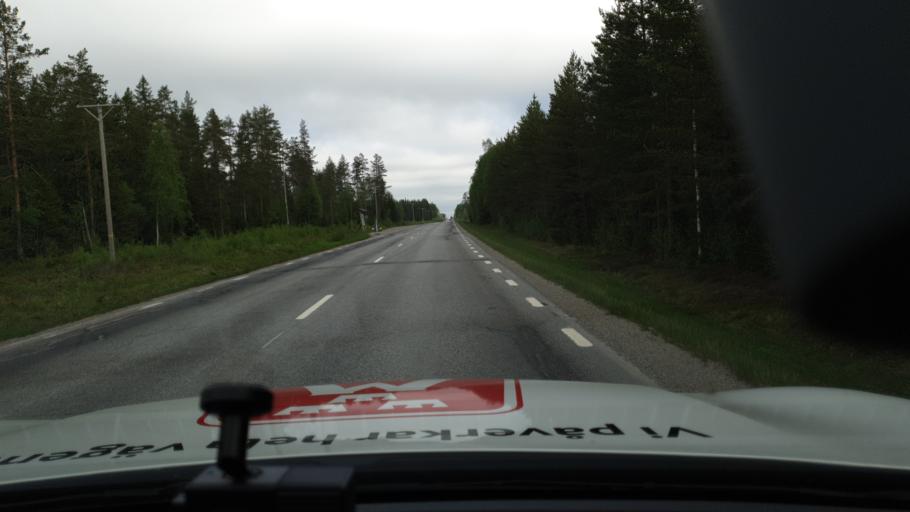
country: SE
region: Vaesterbotten
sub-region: Umea Kommun
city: Roback
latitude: 63.8955
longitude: 20.1977
